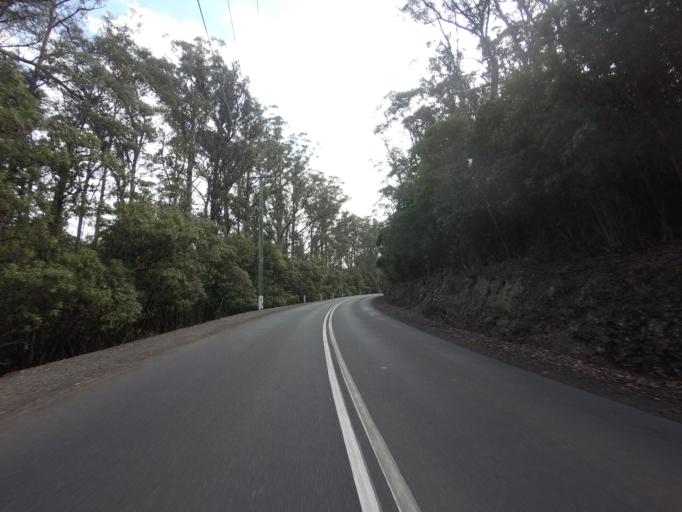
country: AU
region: Tasmania
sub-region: Hobart
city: Dynnyrne
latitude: -42.9209
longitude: 147.2668
